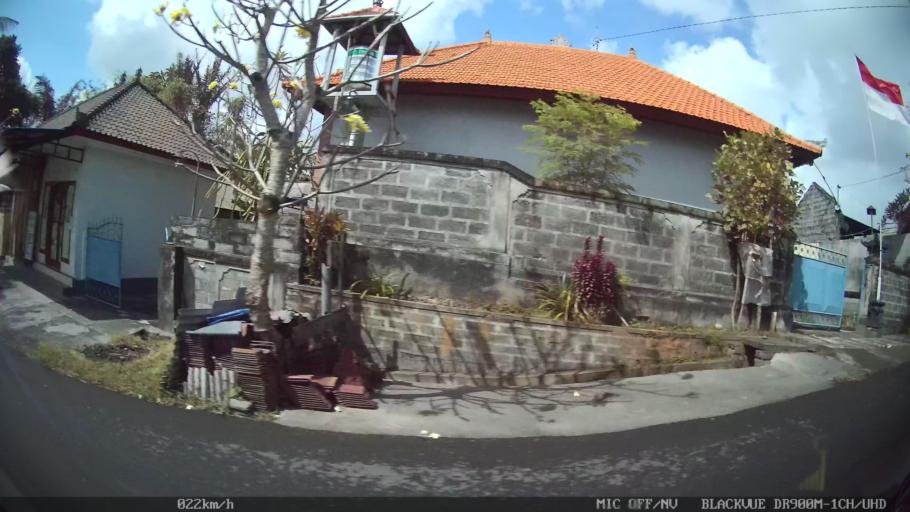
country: ID
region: Bali
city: Banjar Karangsuling
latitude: -8.5988
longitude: 115.2033
